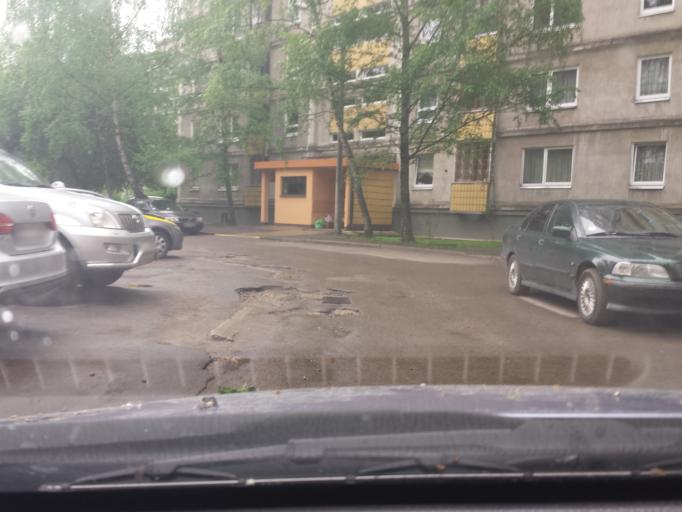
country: LV
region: Riga
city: Riga
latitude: 56.9502
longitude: 24.1900
